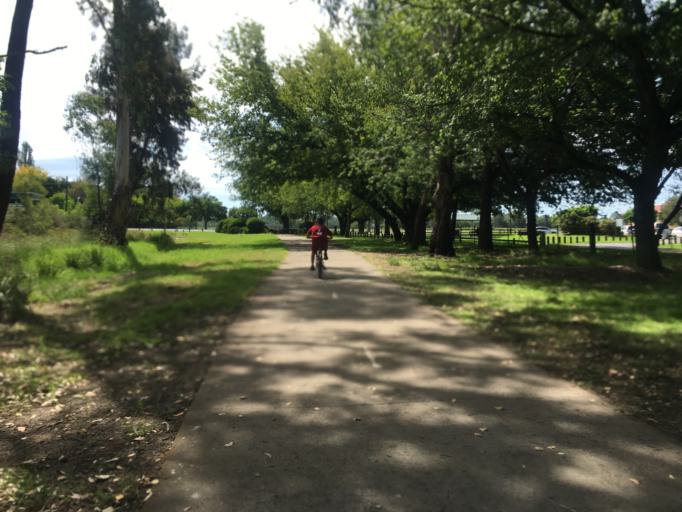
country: AU
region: New South Wales
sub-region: Camden
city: Elderslie
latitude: -34.0544
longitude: 150.7007
